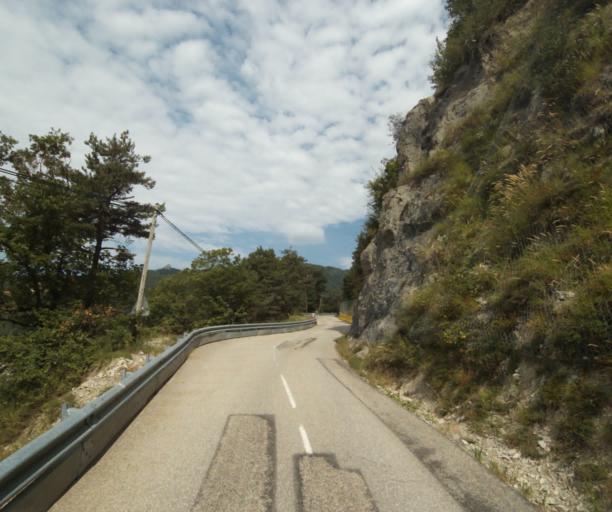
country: FR
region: Rhone-Alpes
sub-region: Departement de l'Isere
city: Le Sappey-en-Chartreuse
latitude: 45.2512
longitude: 5.7421
